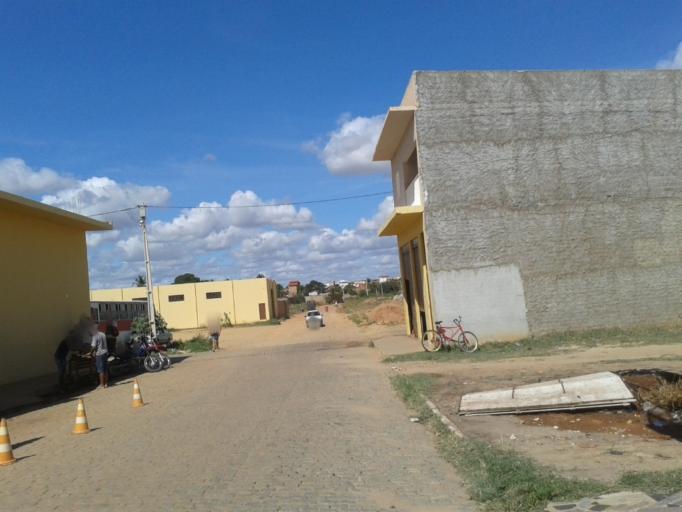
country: BR
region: Bahia
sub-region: Livramento Do Brumado
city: Livramento do Brumado
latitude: -13.6514
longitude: -41.8440
